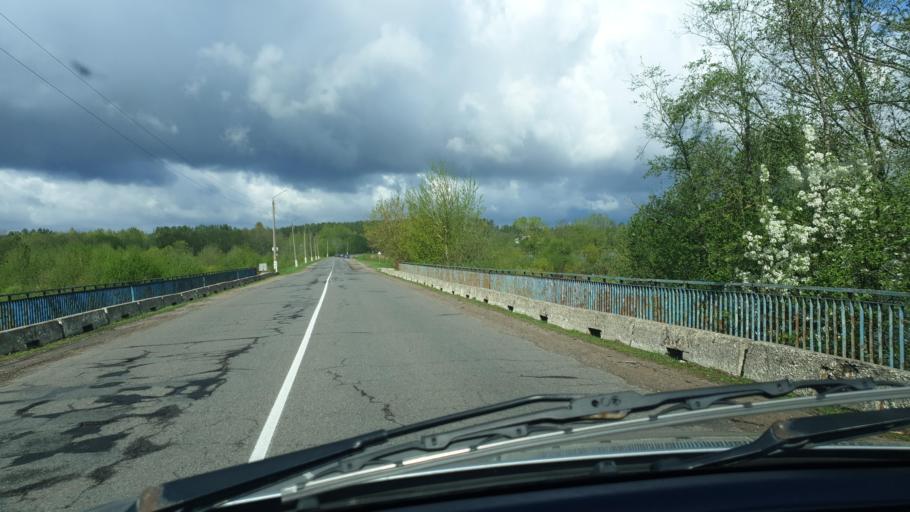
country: BY
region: Vitebsk
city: Lyepyel'
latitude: 54.8768
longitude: 28.6686
